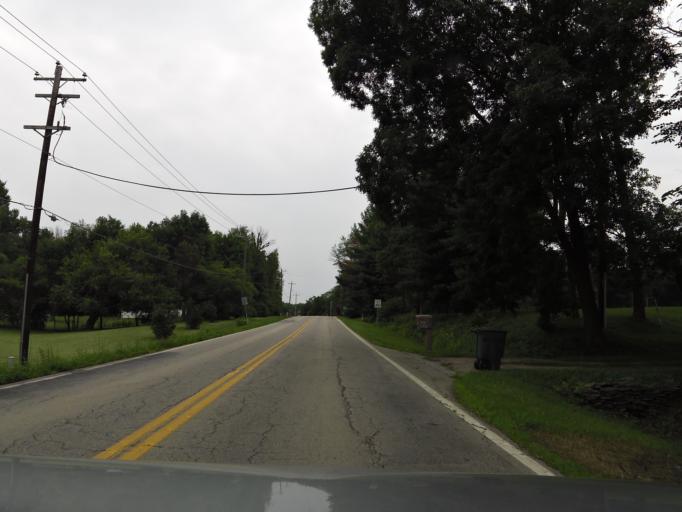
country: US
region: Ohio
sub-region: Clinton County
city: Blanchester
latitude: 39.2845
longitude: -83.9122
